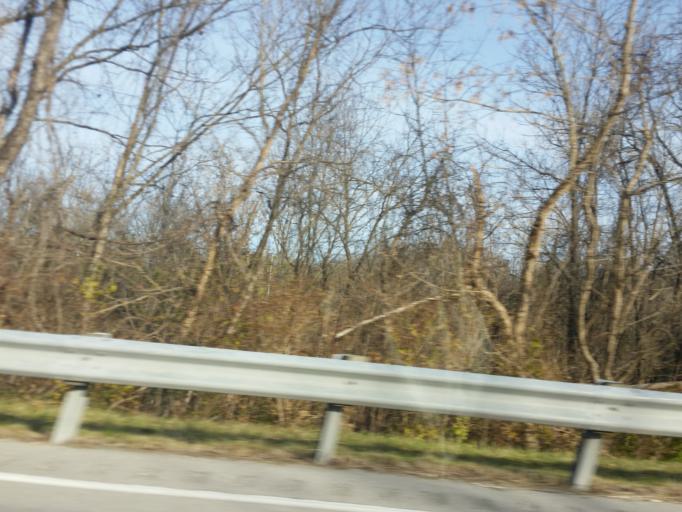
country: US
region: Kentucky
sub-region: Harrison County
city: Cynthiana
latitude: 38.4911
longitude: -84.2841
